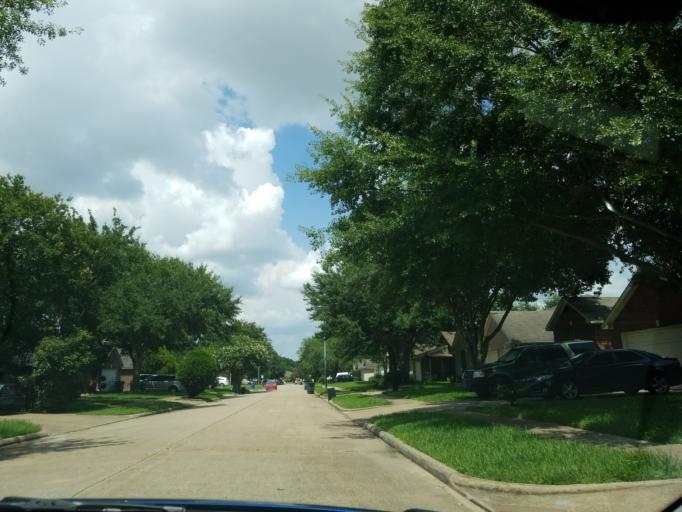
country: US
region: Texas
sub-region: Harris County
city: Cypress
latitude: 29.8714
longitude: -95.7333
